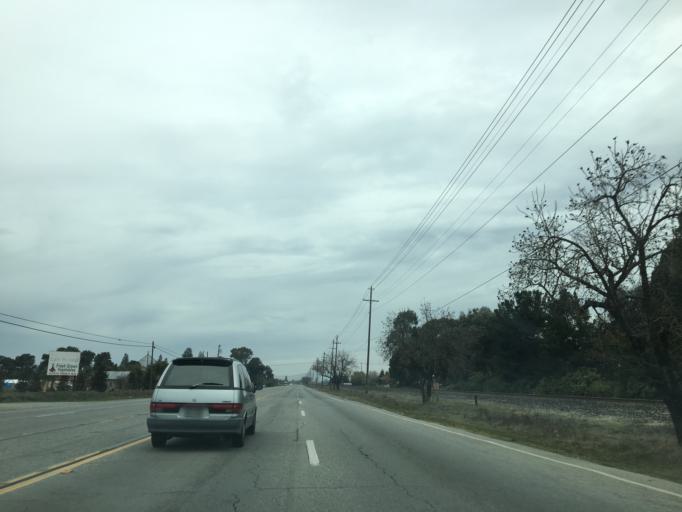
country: US
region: California
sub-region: Santa Clara County
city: San Martin
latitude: 37.0573
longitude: -121.5943
